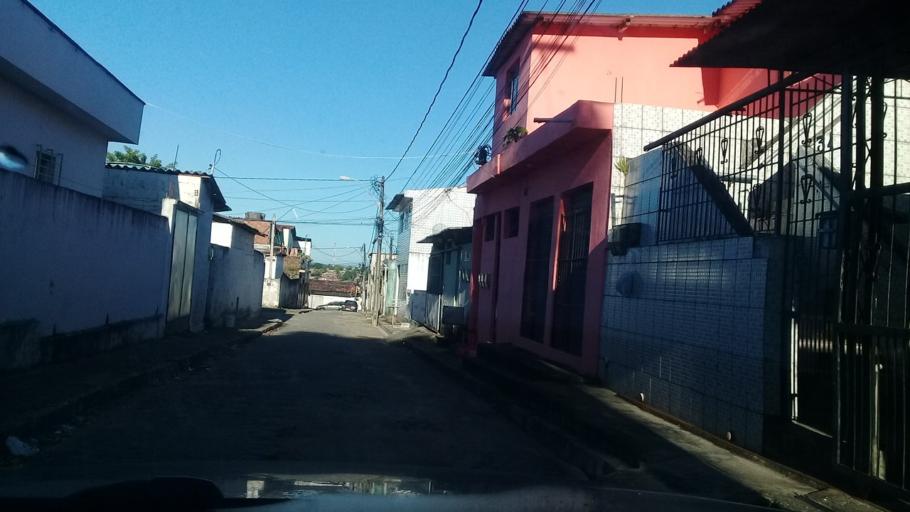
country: BR
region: Pernambuco
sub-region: Jaboatao Dos Guararapes
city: Jaboatao dos Guararapes
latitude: -8.1198
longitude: -34.9563
